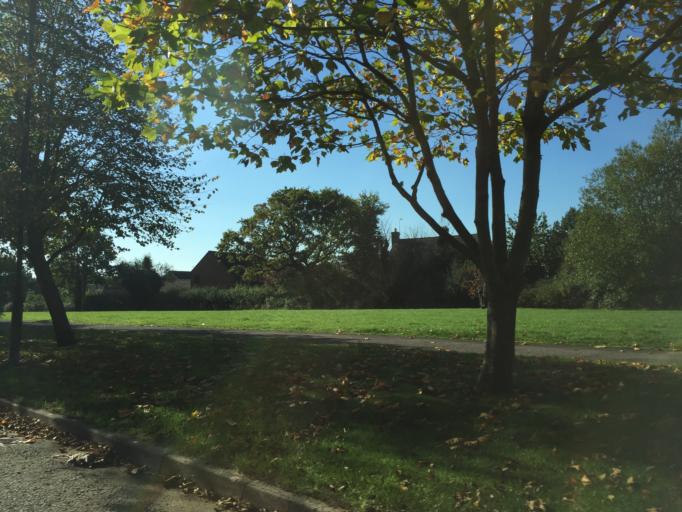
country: GB
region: England
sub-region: South Gloucestershire
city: Yate
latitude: 51.5543
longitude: -2.4204
